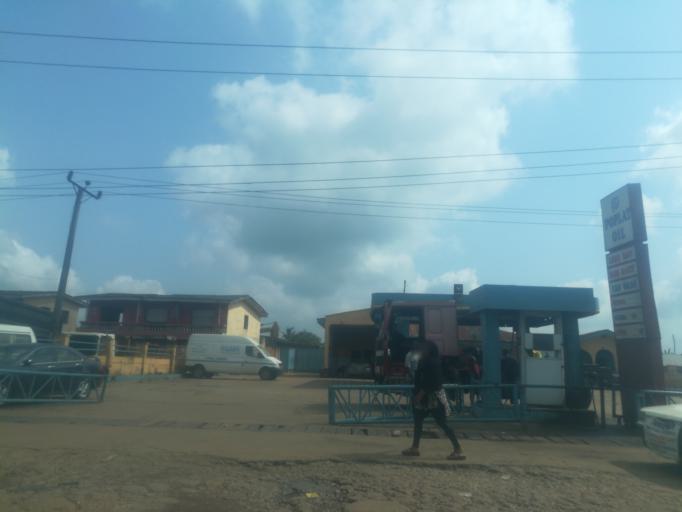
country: NG
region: Oyo
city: Moniya
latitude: 7.4587
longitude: 3.9187
